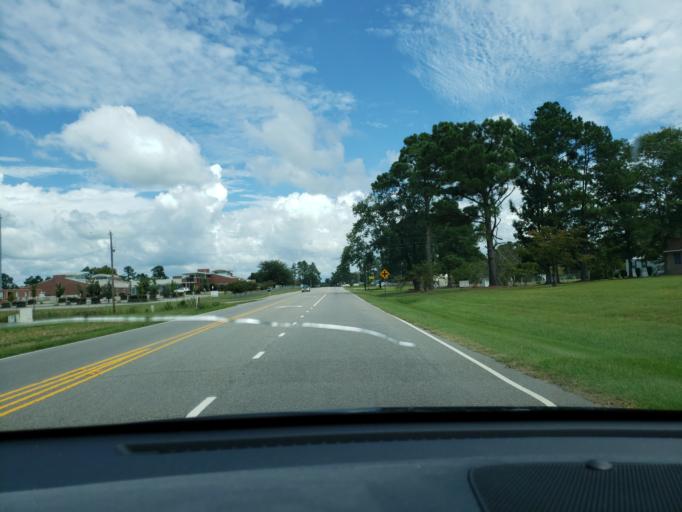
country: US
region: North Carolina
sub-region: Columbus County
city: Brunswick
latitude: 34.2020
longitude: -78.7643
